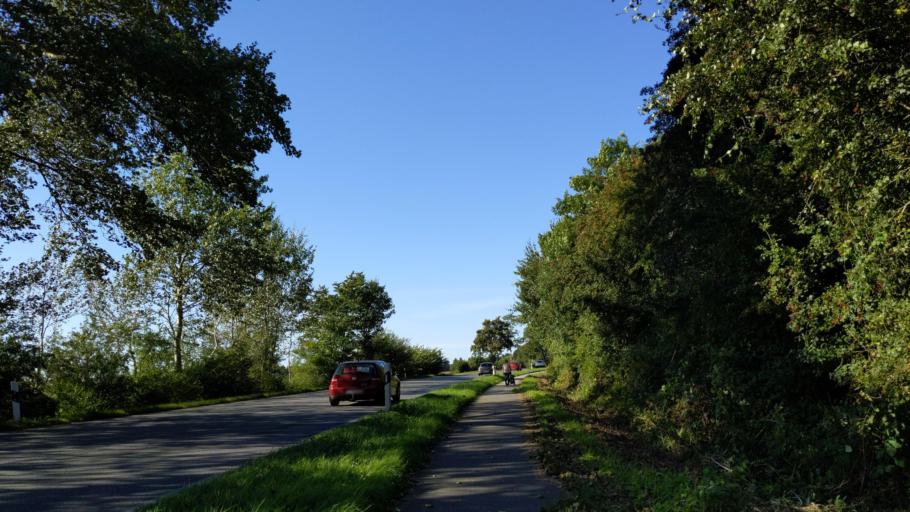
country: DE
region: Schleswig-Holstein
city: Ahrensbok
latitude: 53.9715
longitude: 10.5943
